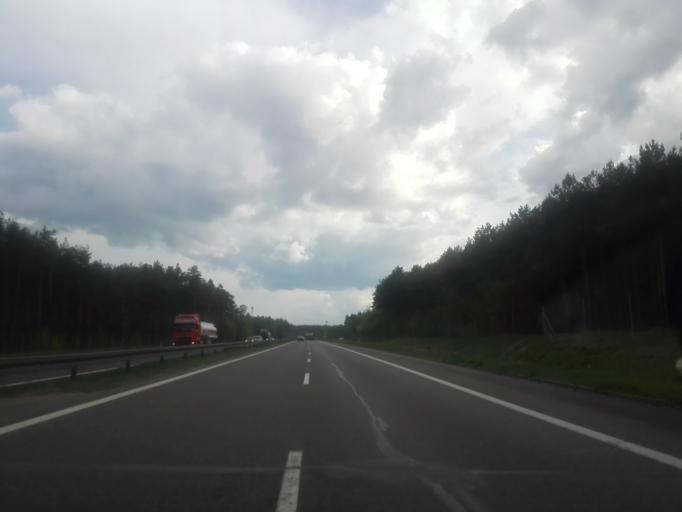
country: PL
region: Masovian Voivodeship
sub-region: Powiat ostrowski
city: Ostrow Mazowiecka
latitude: 52.7959
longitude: 21.8681
